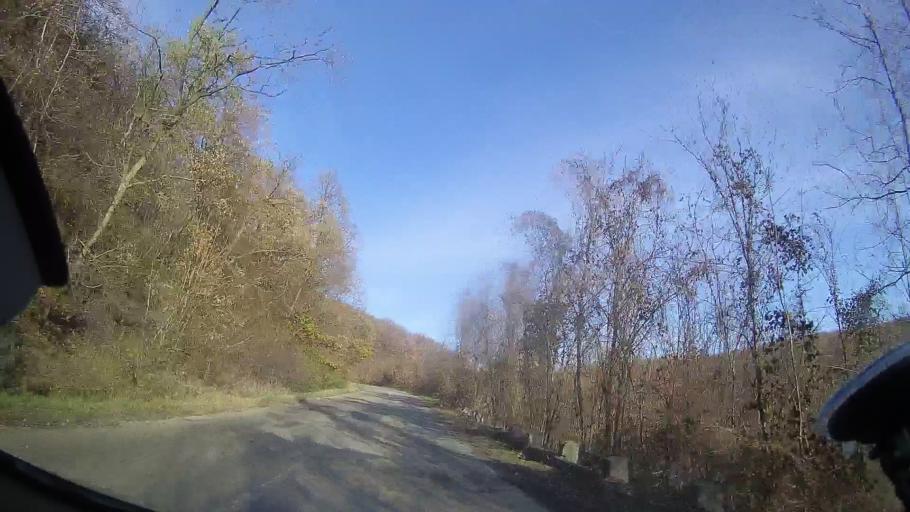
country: RO
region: Bihor
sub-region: Comuna Tileagd
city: Tileagd
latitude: 47.0972
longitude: 22.2410
